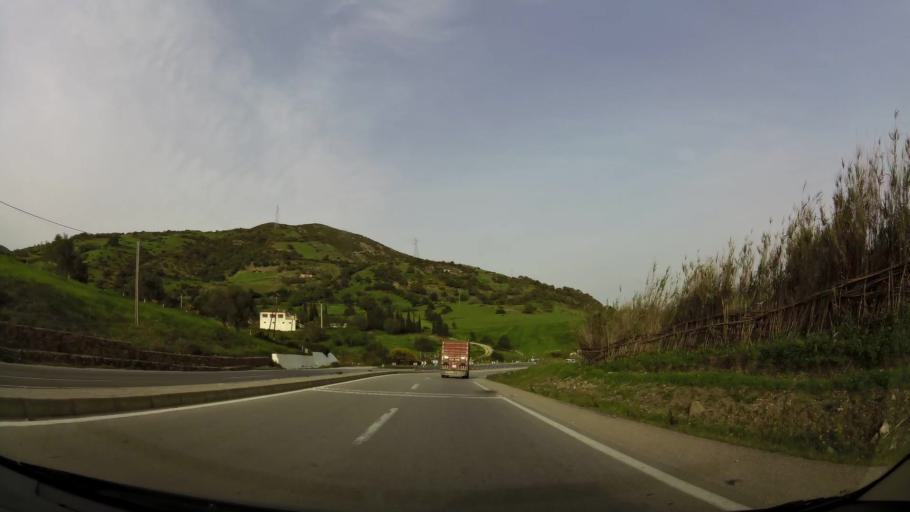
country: MA
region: Tanger-Tetouan
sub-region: Tetouan
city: Saddina
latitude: 35.5503
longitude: -5.5445
